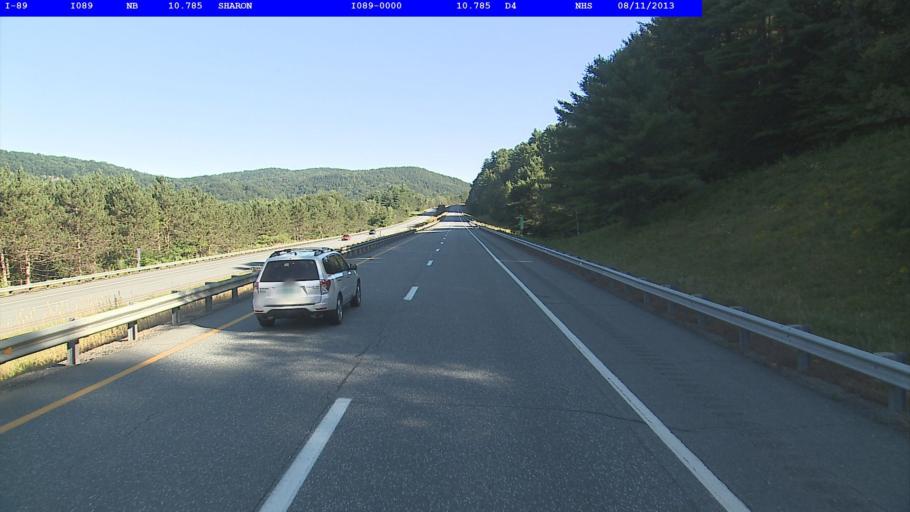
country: US
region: Vermont
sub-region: Windsor County
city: Woodstock
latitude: 43.7511
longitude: -72.4447
